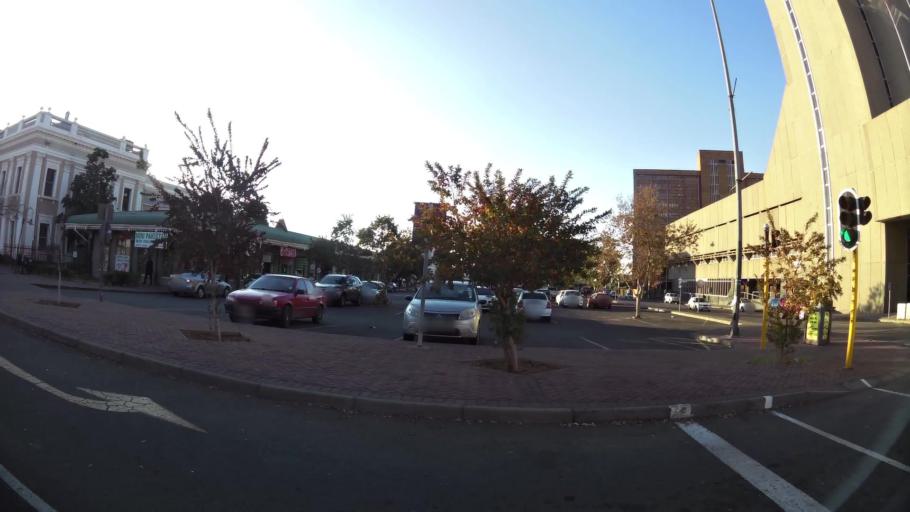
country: ZA
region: Northern Cape
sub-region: Frances Baard District Municipality
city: Kimberley
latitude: -28.7383
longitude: 24.7648
